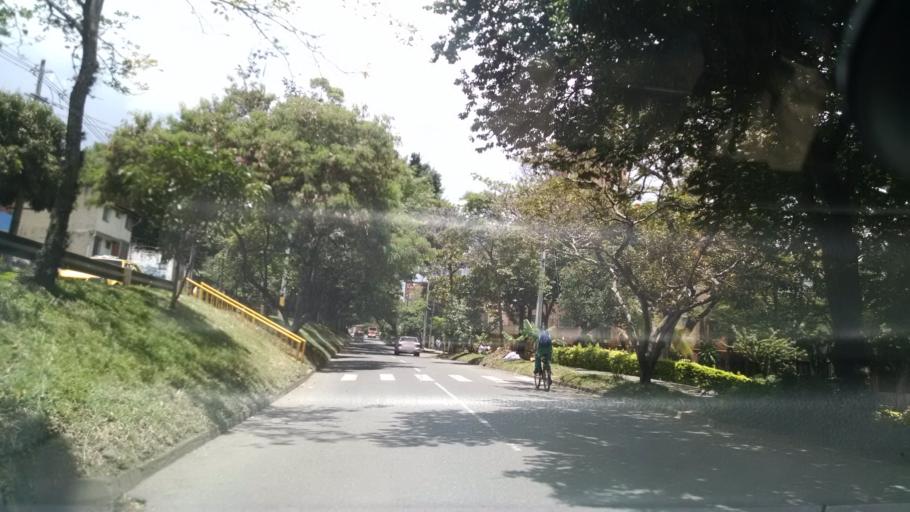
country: CO
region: Antioquia
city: Medellin
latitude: 6.2627
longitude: -75.6014
